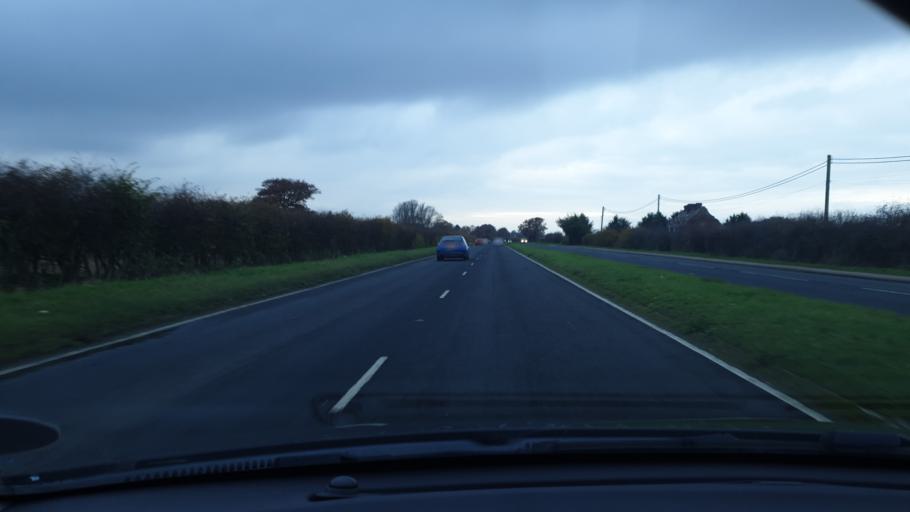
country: GB
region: England
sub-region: Essex
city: Wivenhoe
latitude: 51.8814
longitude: 0.9632
